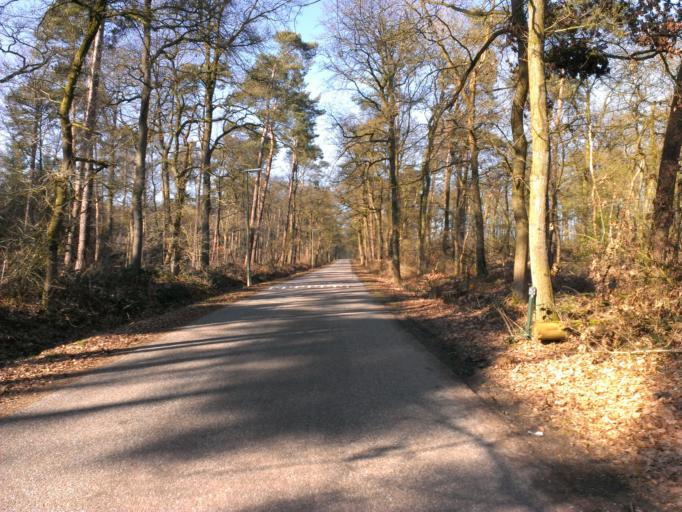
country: NL
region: Overijssel
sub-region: Gemeente Almelo
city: Almelo
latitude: 52.3307
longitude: 6.6823
